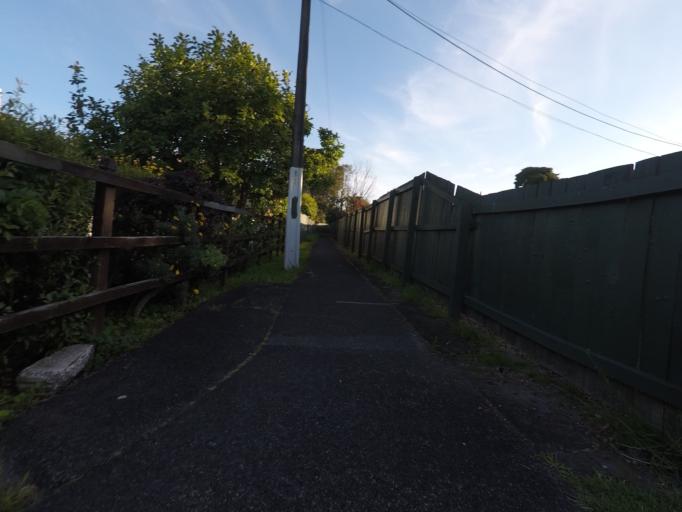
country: NZ
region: Auckland
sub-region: Auckland
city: Rosebank
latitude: -36.8443
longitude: 174.6499
